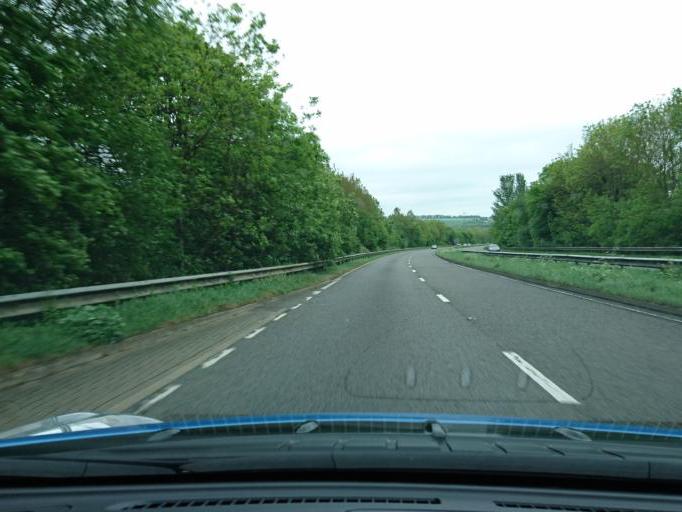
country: GB
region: England
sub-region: Oxfordshire
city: Boars Hill
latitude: 51.7403
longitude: -1.3261
